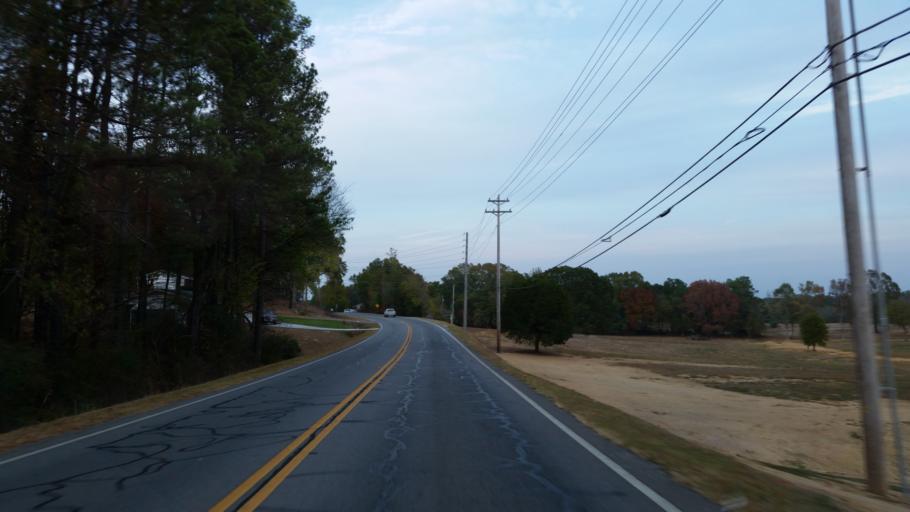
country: US
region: Georgia
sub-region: Gordon County
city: Calhoun
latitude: 34.5884
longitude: -84.9353
